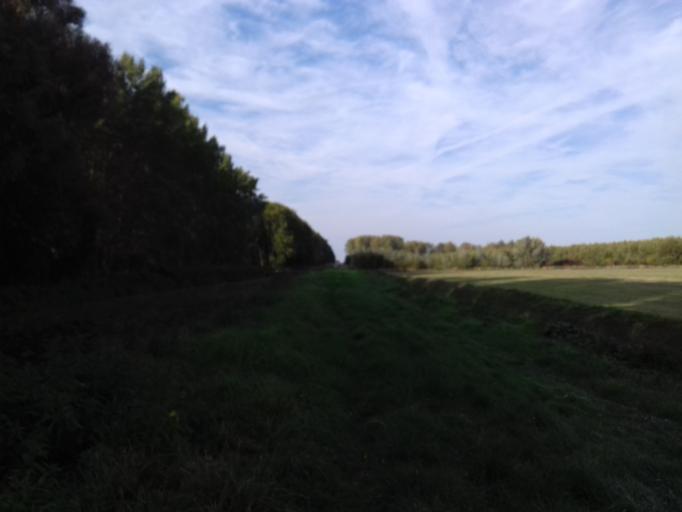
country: NL
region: Gelderland
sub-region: Gemeente Culemborg
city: Culemborg
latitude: 51.9167
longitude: 5.2385
